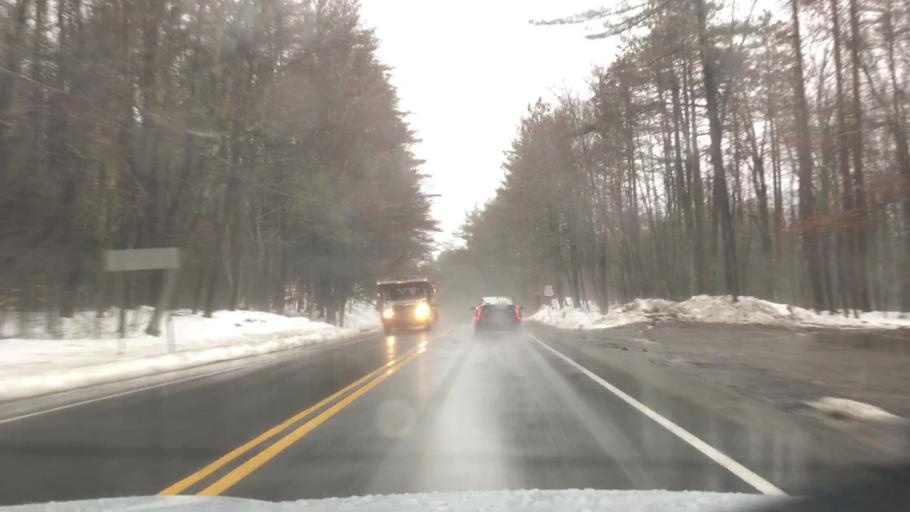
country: US
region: Massachusetts
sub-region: Franklin County
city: Shutesbury
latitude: 42.4495
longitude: -72.3876
